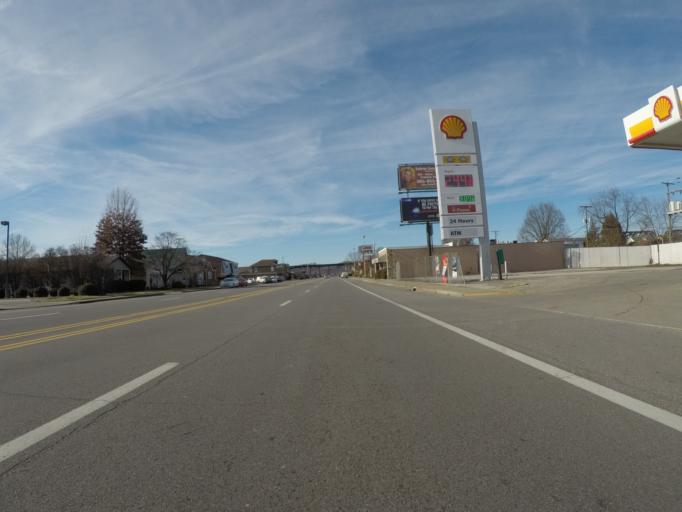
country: US
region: West Virginia
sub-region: Wayne County
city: Kenova
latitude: 38.3993
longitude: -82.5713
